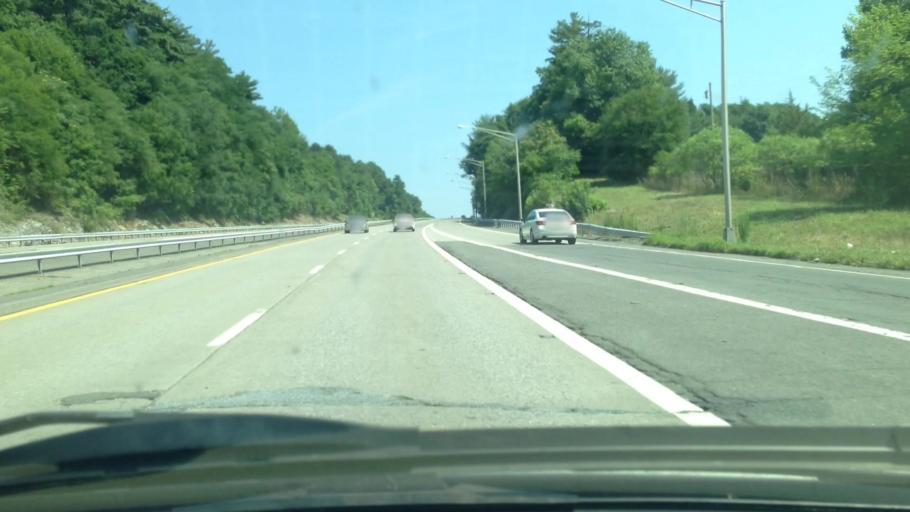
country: US
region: New York
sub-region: Ulster County
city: Kingston
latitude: 41.9301
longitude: -73.9856
